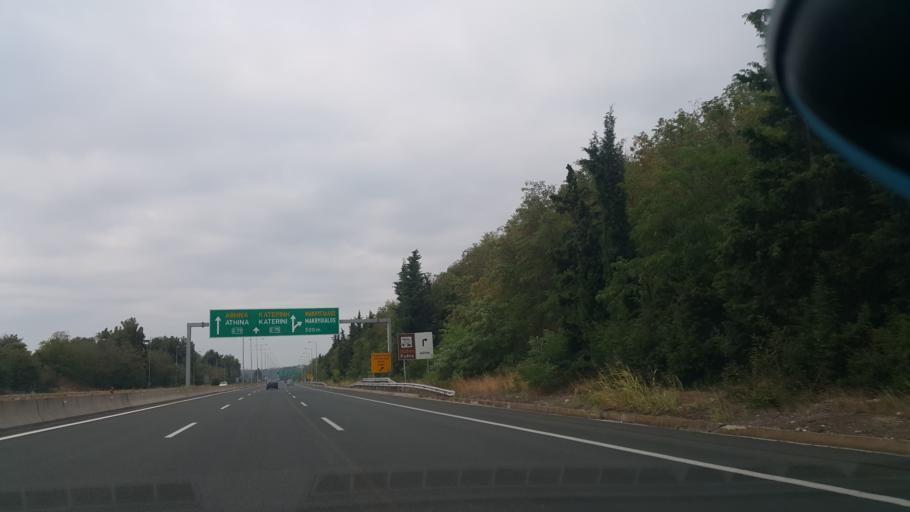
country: GR
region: Central Macedonia
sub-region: Nomos Pierias
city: Makrygialos
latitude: 40.4272
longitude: 22.5889
